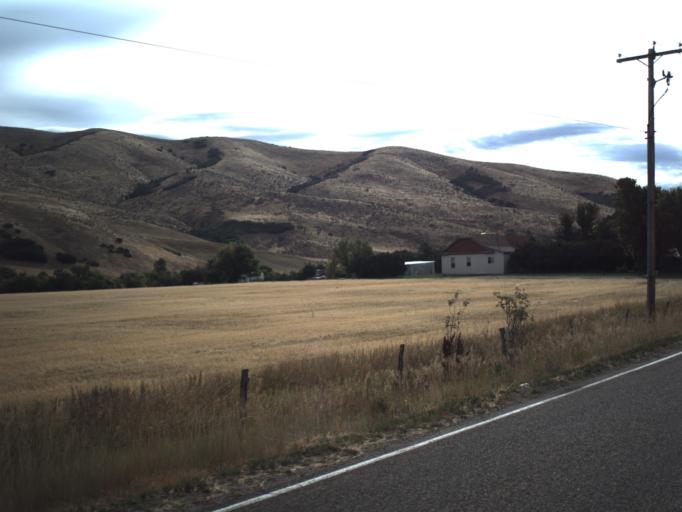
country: US
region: Utah
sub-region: Morgan County
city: Morgan
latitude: 40.9623
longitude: -111.6695
